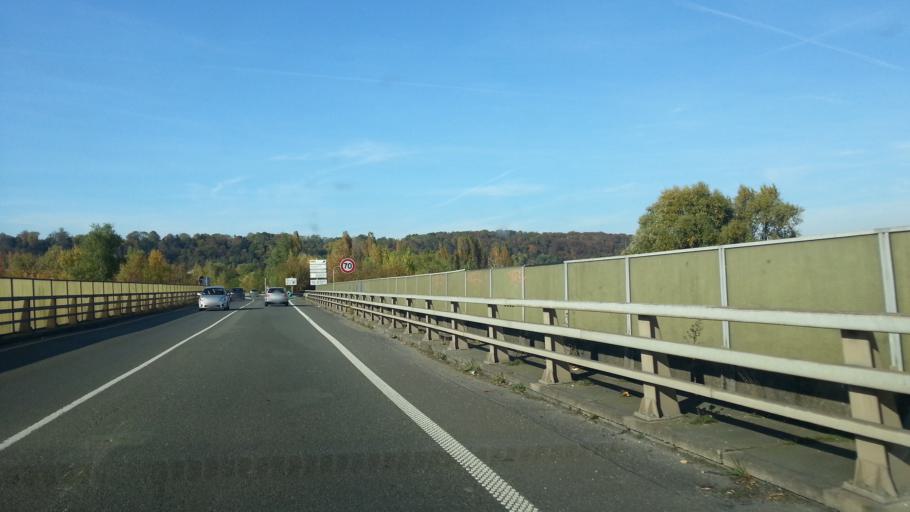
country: FR
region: Picardie
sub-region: Departement de l'Oise
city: Montataire
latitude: 49.2550
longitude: 2.4539
